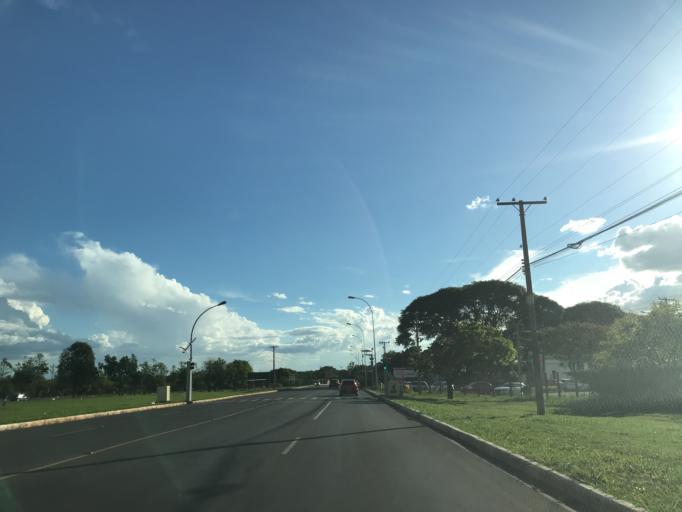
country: BR
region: Federal District
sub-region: Brasilia
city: Brasilia
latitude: -15.7958
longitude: -47.9104
